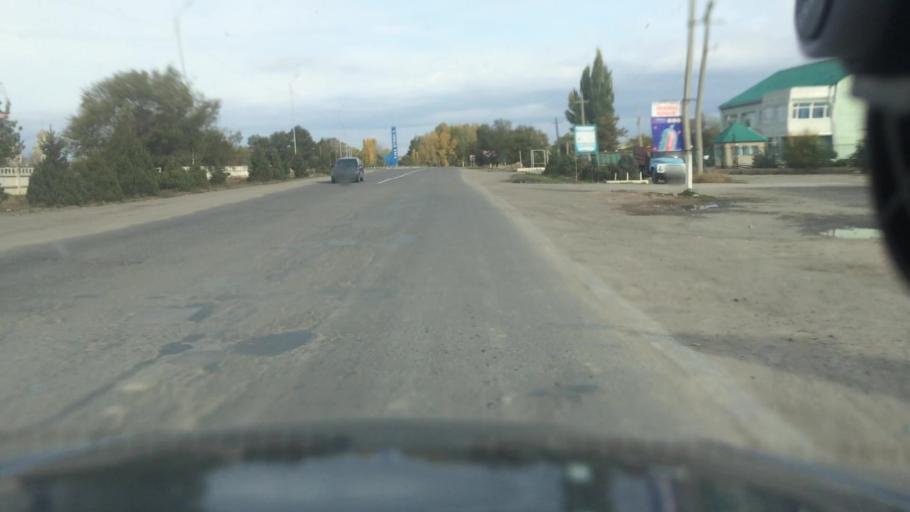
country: KG
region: Ysyk-Koel
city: Karakol
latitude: 42.5305
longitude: 78.3828
